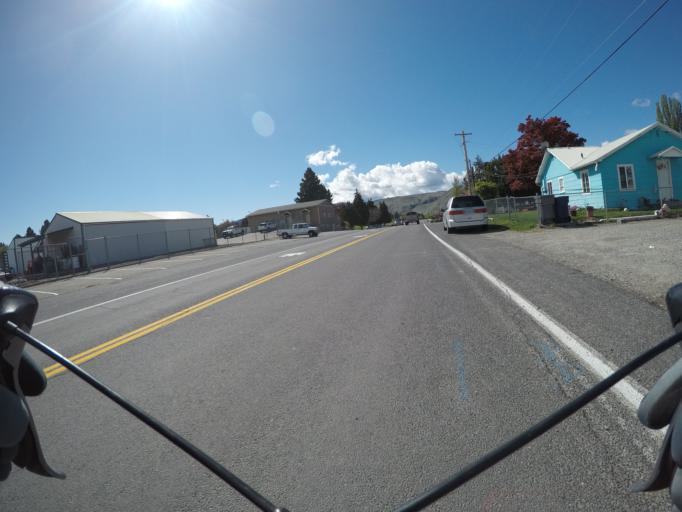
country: US
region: Washington
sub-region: Douglas County
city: East Wenatchee Bench
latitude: 47.4094
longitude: -120.2771
